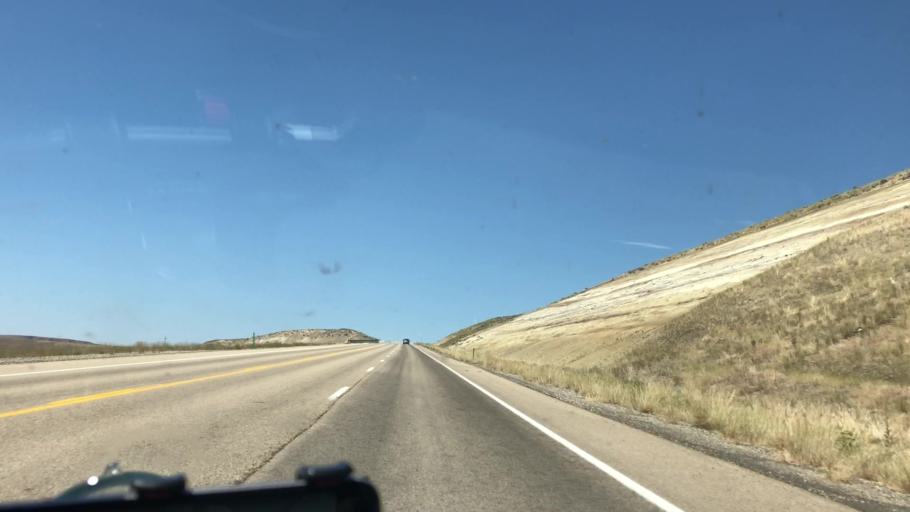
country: US
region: Idaho
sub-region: Owyhee County
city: Marsing
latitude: 43.2897
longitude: -116.9859
